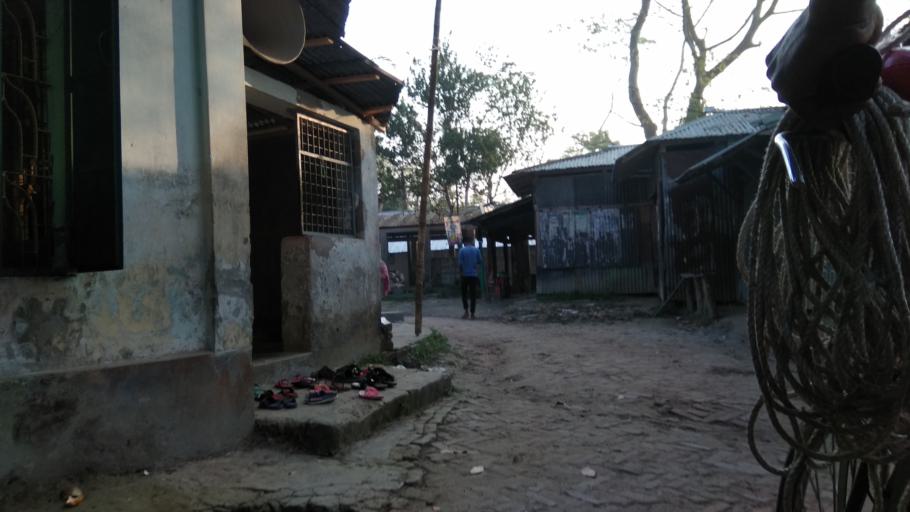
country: BD
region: Barisal
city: Mehendiganj
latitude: 22.9319
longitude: 90.4122
